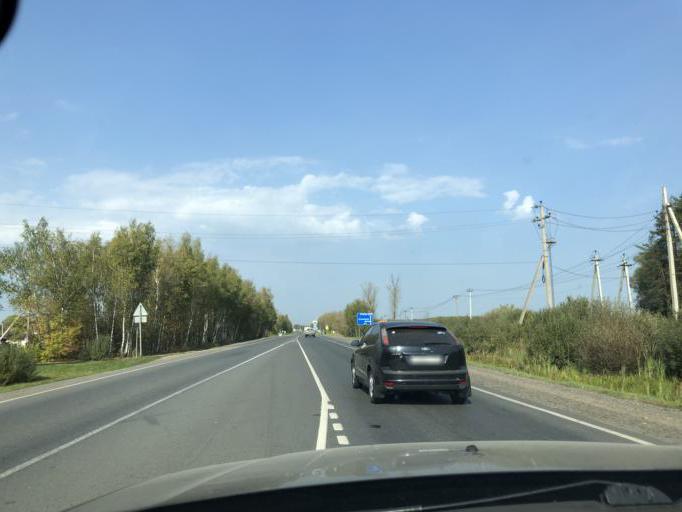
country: RU
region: Moskovskaya
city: L'vovskiy
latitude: 55.3405
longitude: 37.4632
